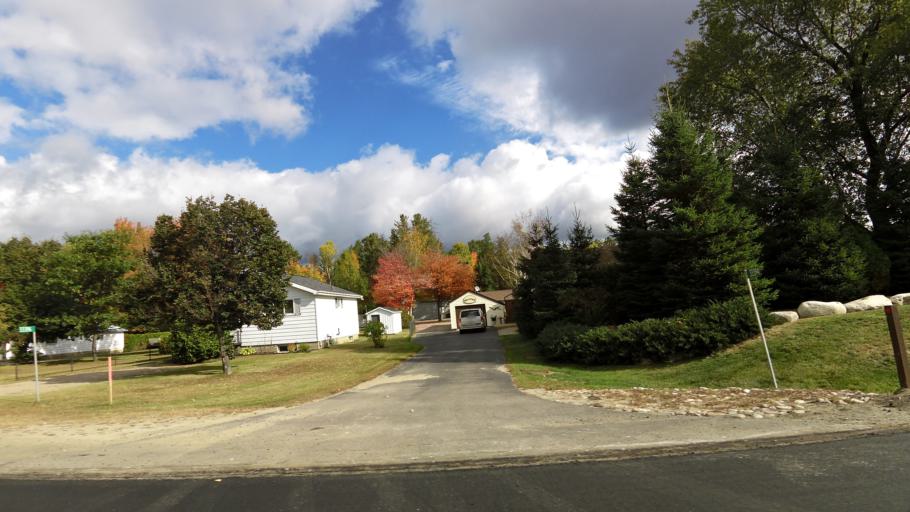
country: CA
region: Ontario
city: Deep River
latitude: 46.1033
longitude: -77.5059
